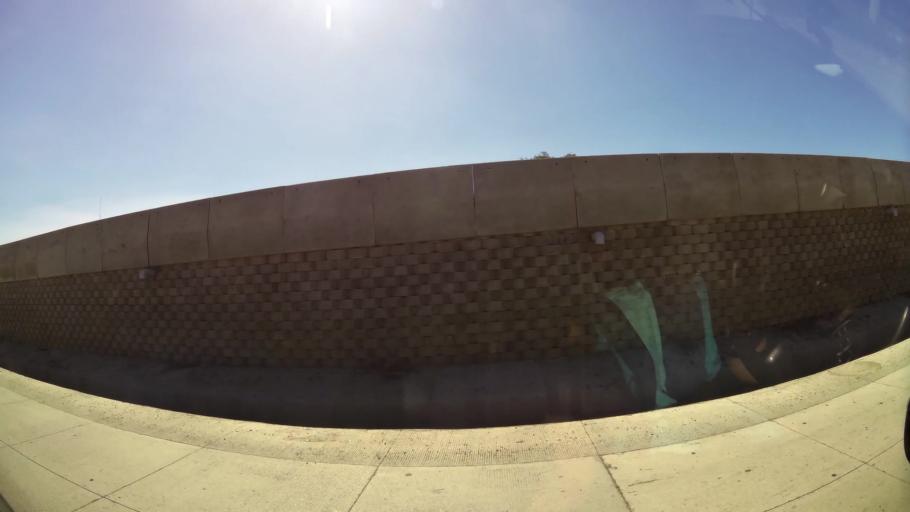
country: CR
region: Guanacaste
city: Liberia
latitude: 10.6299
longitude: -85.4456
